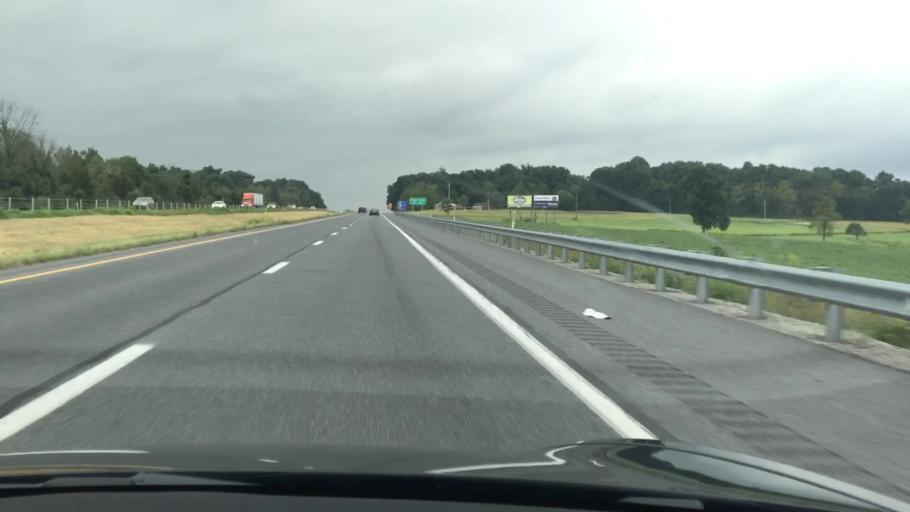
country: US
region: Pennsylvania
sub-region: Adams County
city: Lake Meade
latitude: 39.9582
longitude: -77.1318
